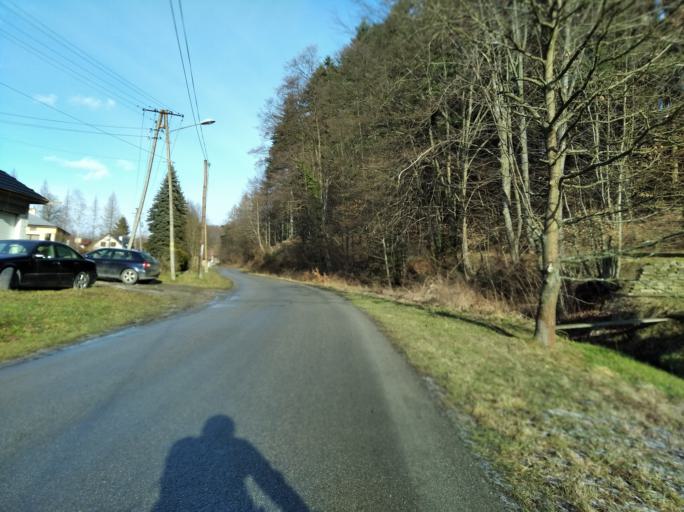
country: PL
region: Subcarpathian Voivodeship
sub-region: Powiat strzyzowski
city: Strzyzow
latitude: 49.8925
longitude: 21.7778
